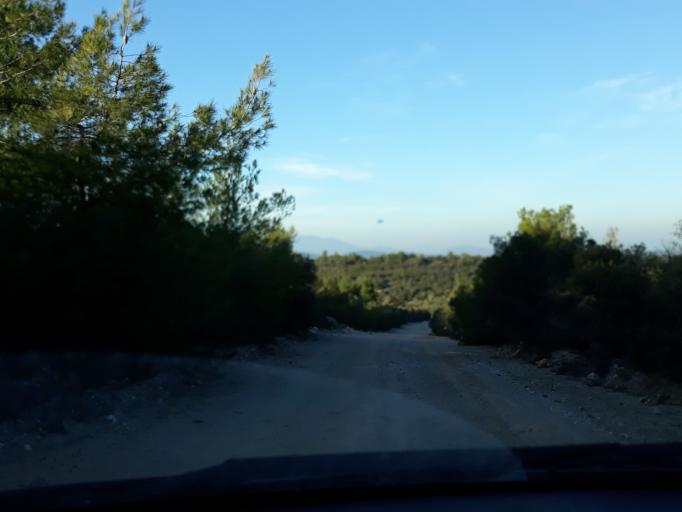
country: GR
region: Central Greece
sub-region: Nomos Voiotias
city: Asopia
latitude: 38.2527
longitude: 23.5312
